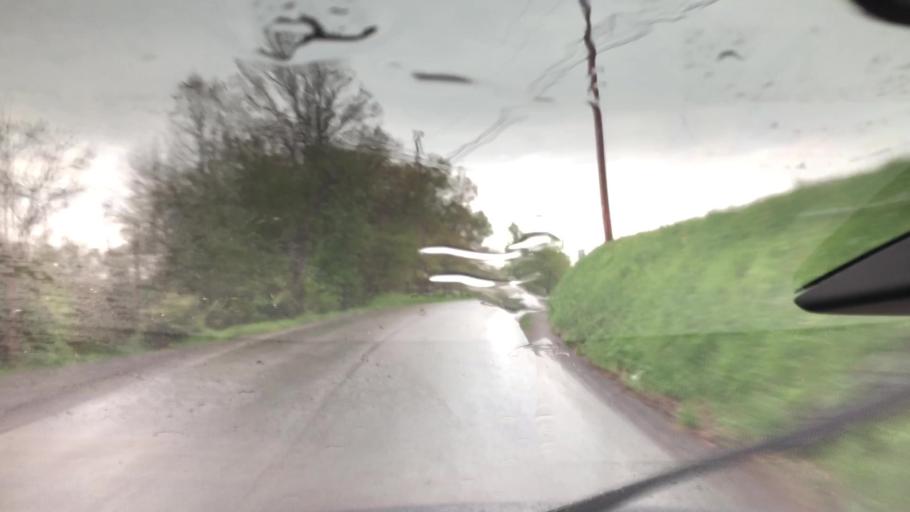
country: US
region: Pennsylvania
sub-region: Butler County
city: Saxonburg
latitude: 40.7524
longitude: -79.8569
